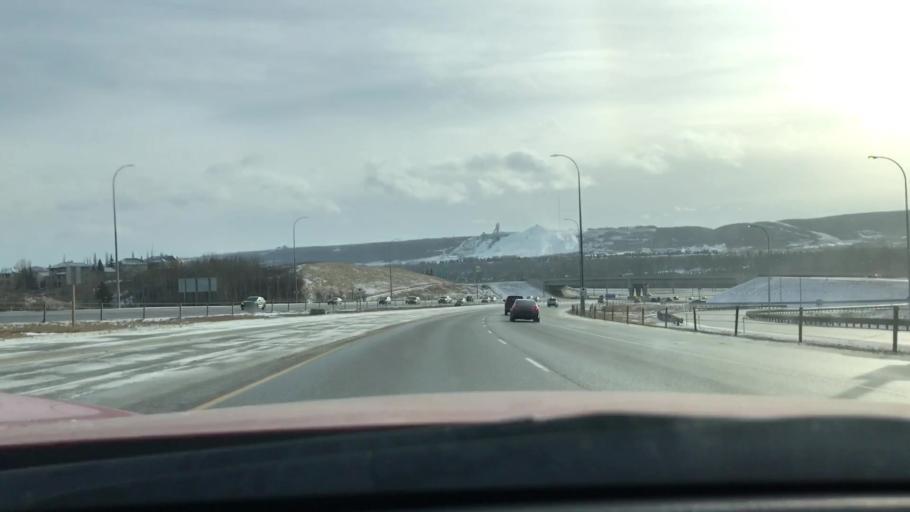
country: CA
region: Alberta
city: Calgary
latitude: 51.1105
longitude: -114.2246
